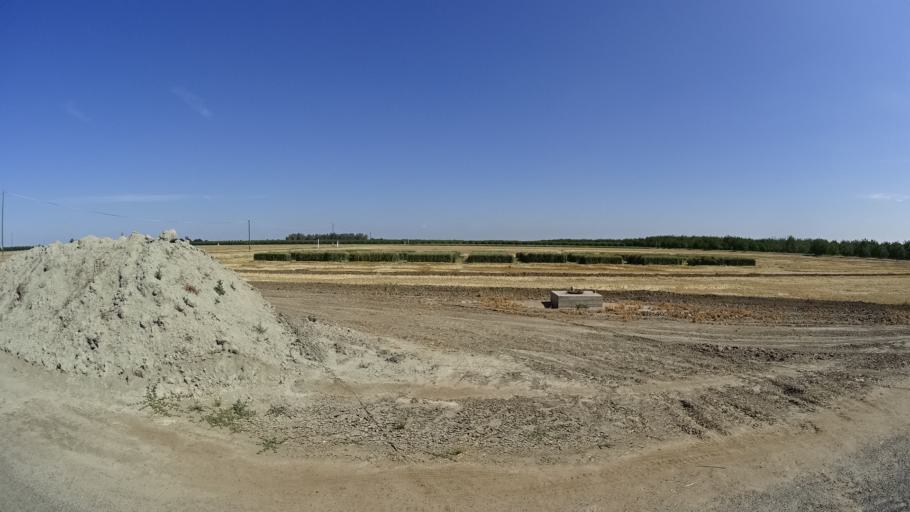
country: US
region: California
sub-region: Kings County
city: Armona
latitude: 36.2548
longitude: -119.7016
